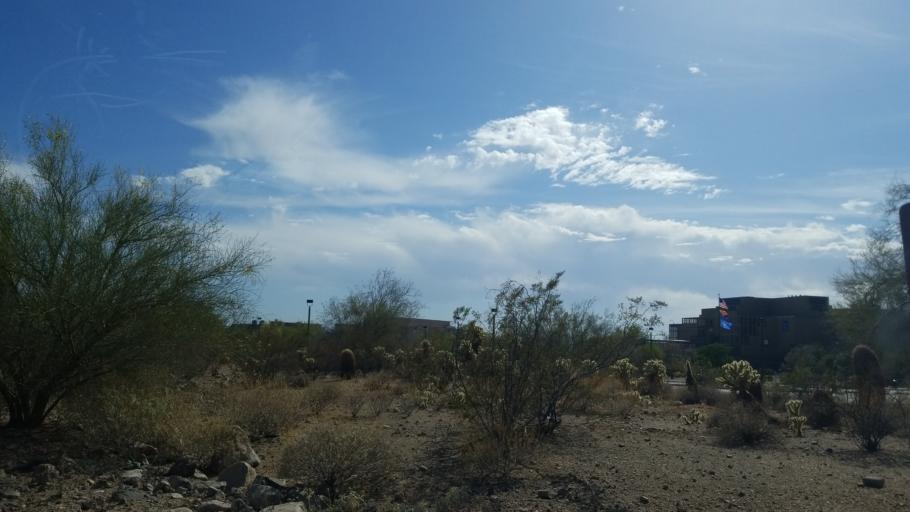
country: US
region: Arizona
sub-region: Maricopa County
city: Fountain Hills
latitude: 33.5863
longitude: -111.7921
